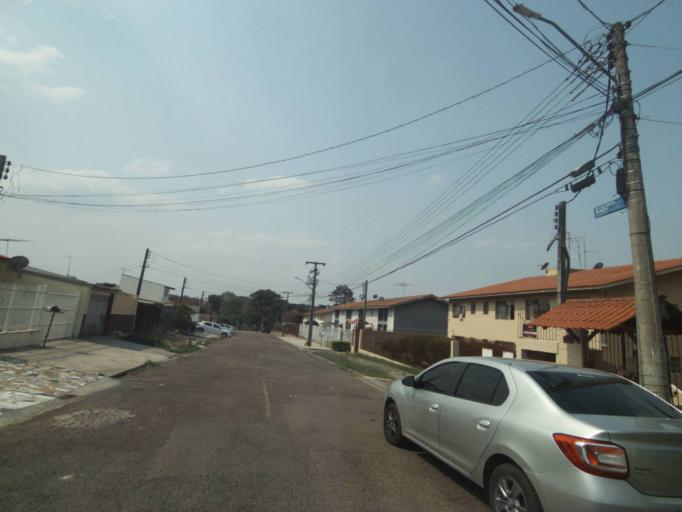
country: BR
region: Parana
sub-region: Sao Jose Dos Pinhais
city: Sao Jose dos Pinhais
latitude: -25.5310
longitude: -49.2429
